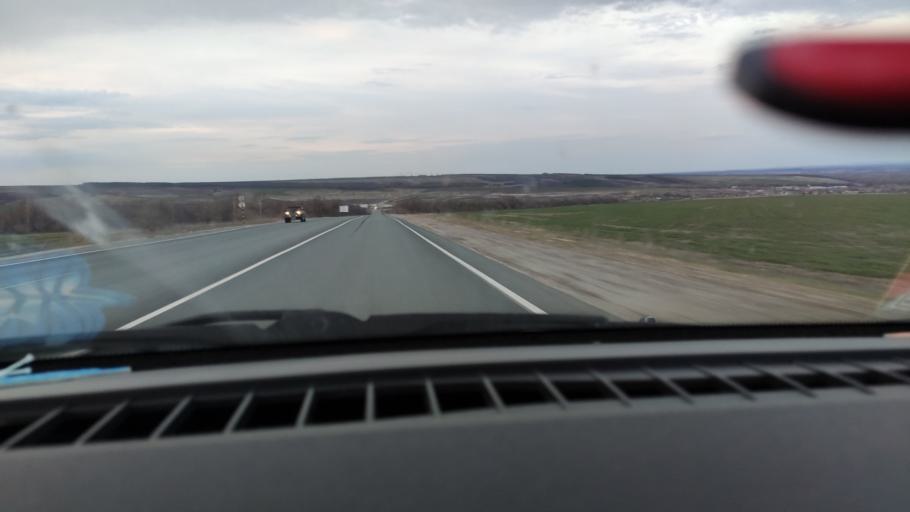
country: RU
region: Saratov
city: Sinodskoye
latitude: 51.9121
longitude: 46.5541
